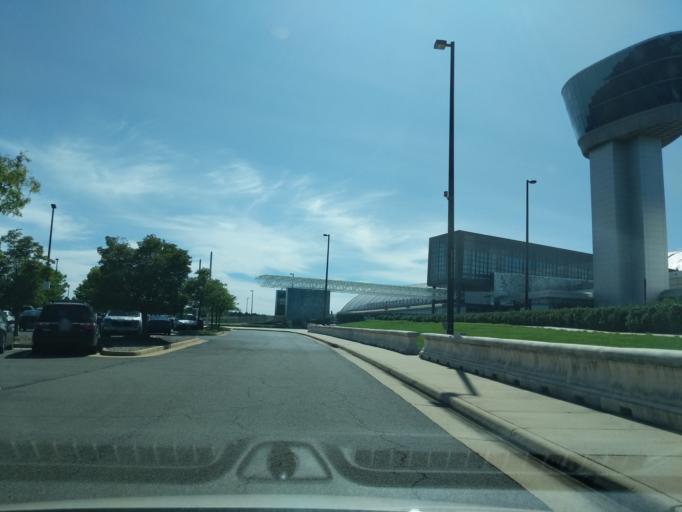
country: US
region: Virginia
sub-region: Fairfax County
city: Chantilly
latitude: 38.9123
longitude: -77.4422
